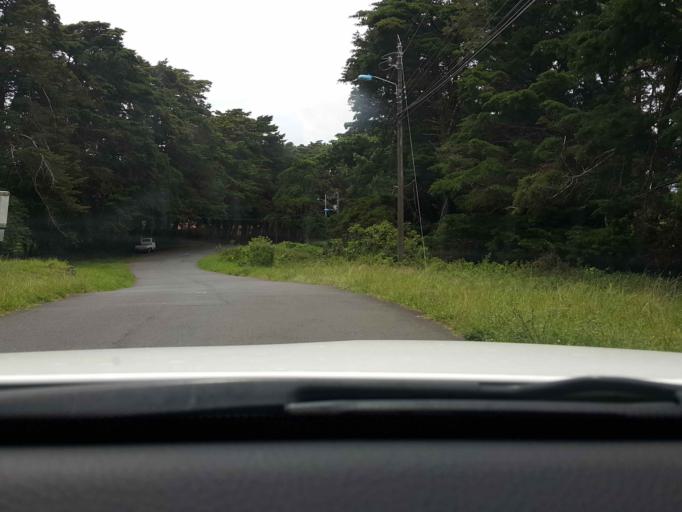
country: CR
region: Heredia
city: San Josecito
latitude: 10.0534
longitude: -84.0888
